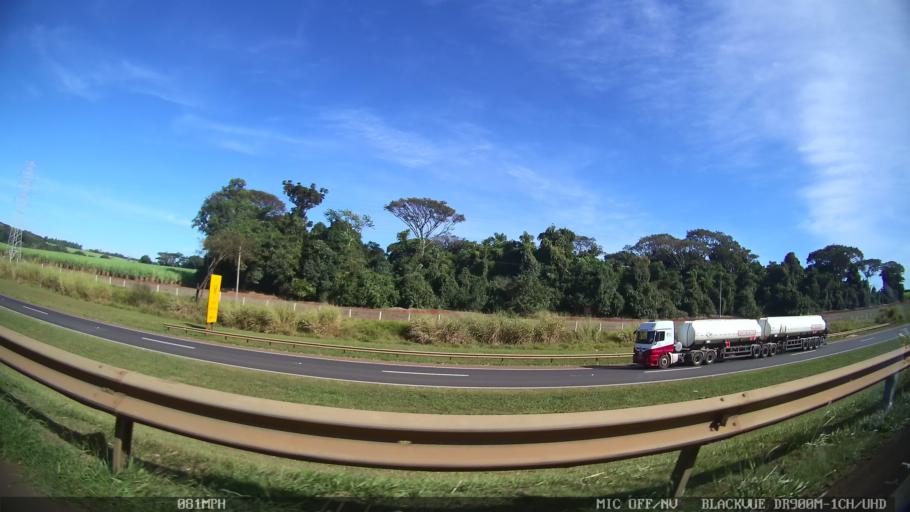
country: BR
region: Sao Paulo
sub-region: Araras
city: Araras
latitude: -22.3047
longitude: -47.3917
